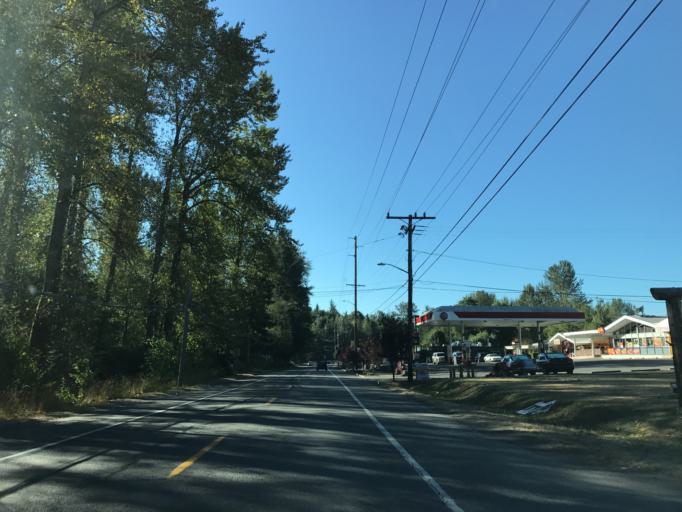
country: US
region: Washington
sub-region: King County
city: Black Diamond
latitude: 47.3196
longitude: -122.0054
